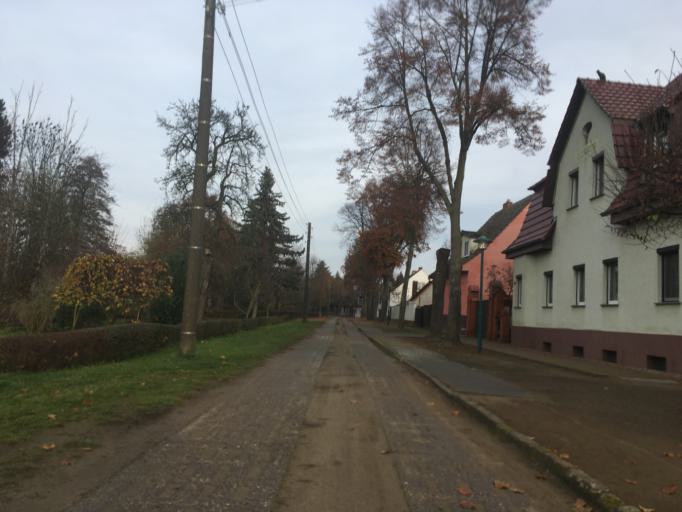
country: DE
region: Brandenburg
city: Neulewin
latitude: 52.7265
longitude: 14.2793
